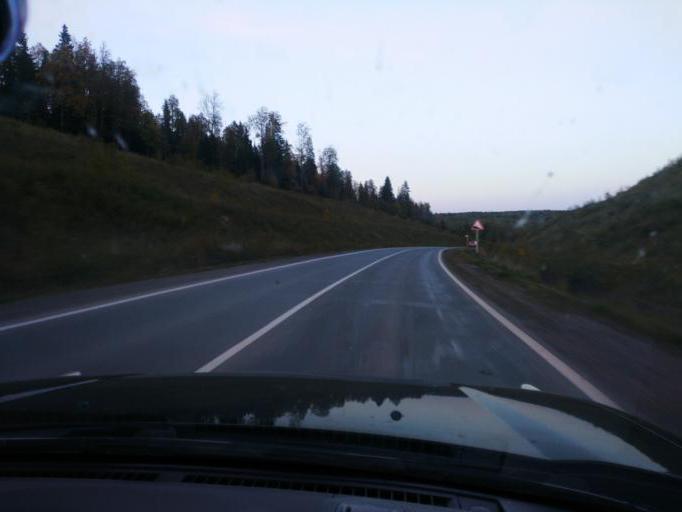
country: RU
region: Perm
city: Sylva
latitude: 58.3026
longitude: 56.7848
